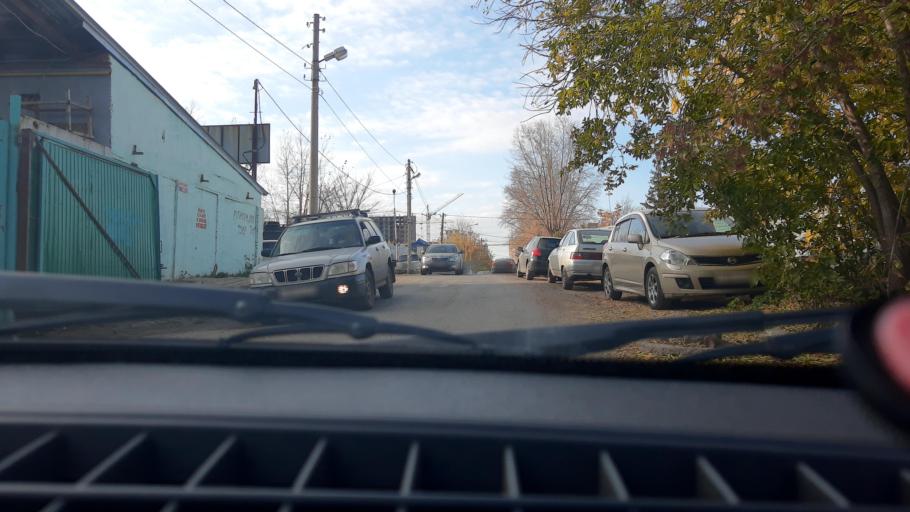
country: RU
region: Bashkortostan
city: Ufa
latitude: 54.7481
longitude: 55.9682
